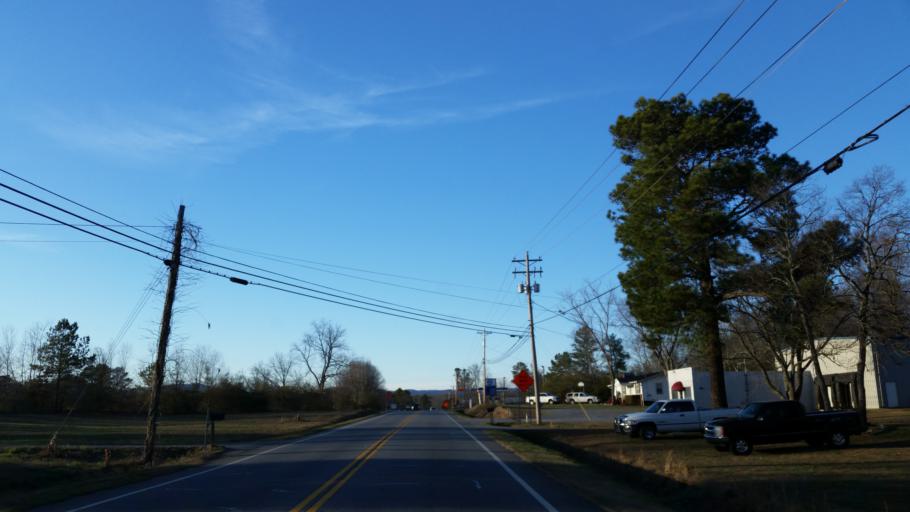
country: US
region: Georgia
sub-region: Whitfield County
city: Dalton
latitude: 34.6421
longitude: -84.9671
